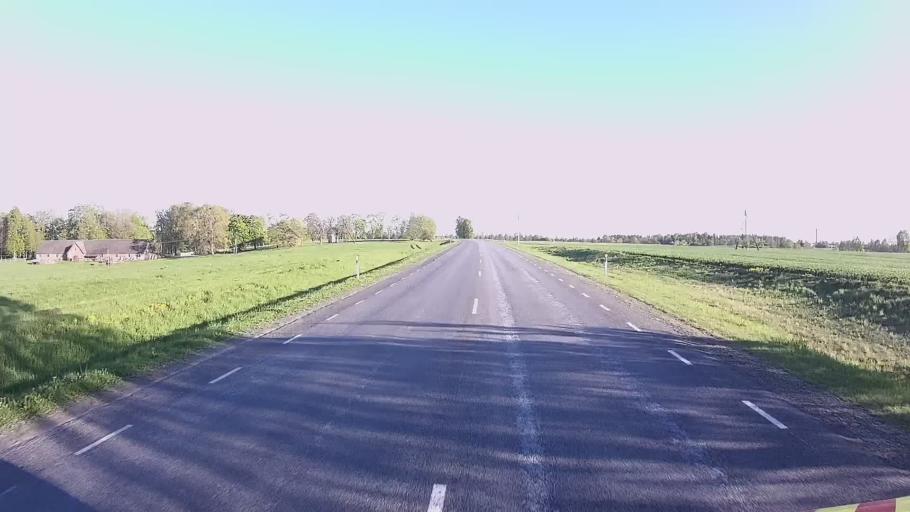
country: EE
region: Viljandimaa
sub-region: Viljandi linn
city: Viljandi
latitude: 58.3985
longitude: 25.5917
